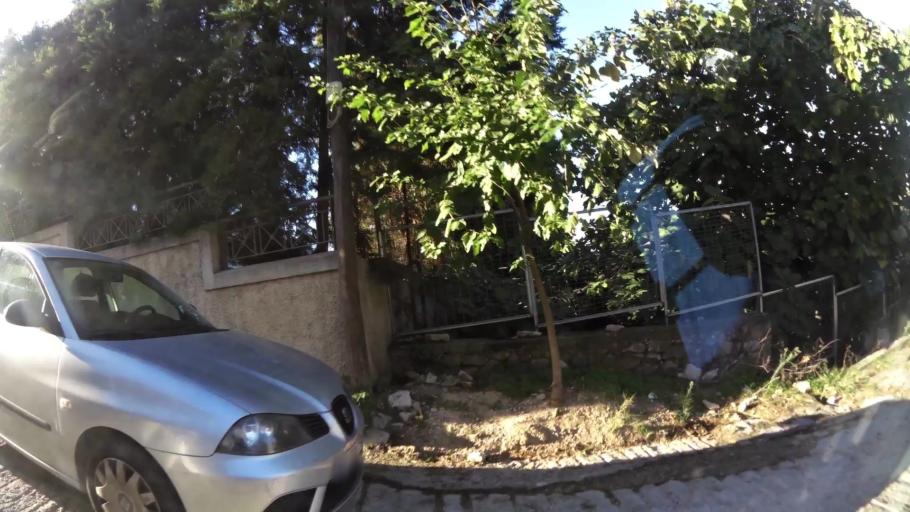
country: GR
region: Attica
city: Pefki
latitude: 38.0550
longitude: 23.7841
